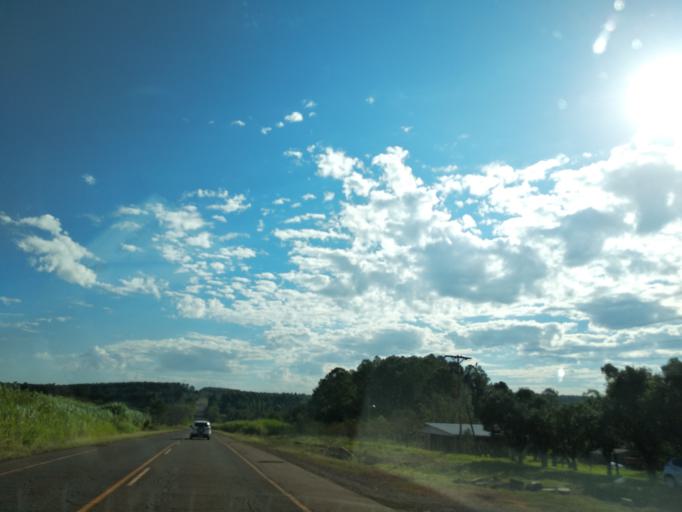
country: AR
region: Misiones
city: Ruiz de Montoya
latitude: -27.0592
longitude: -55.0282
